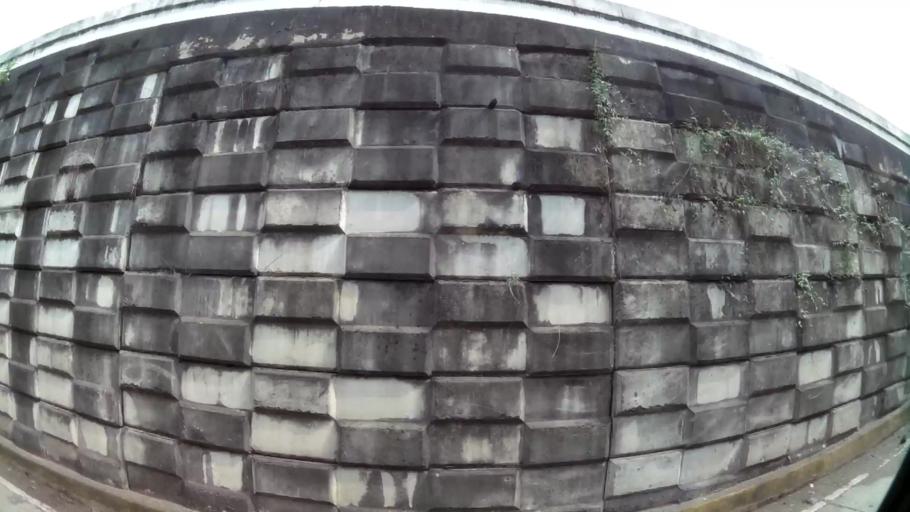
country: PA
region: Panama
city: Tocumen
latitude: 9.1022
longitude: -79.3666
